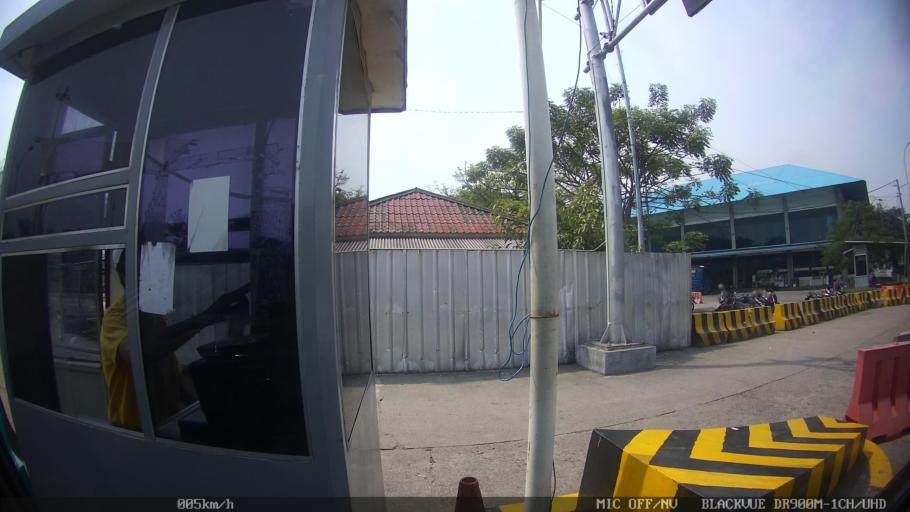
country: ID
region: Banten
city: Kubangkepuh
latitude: -5.9357
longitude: 106.0008
